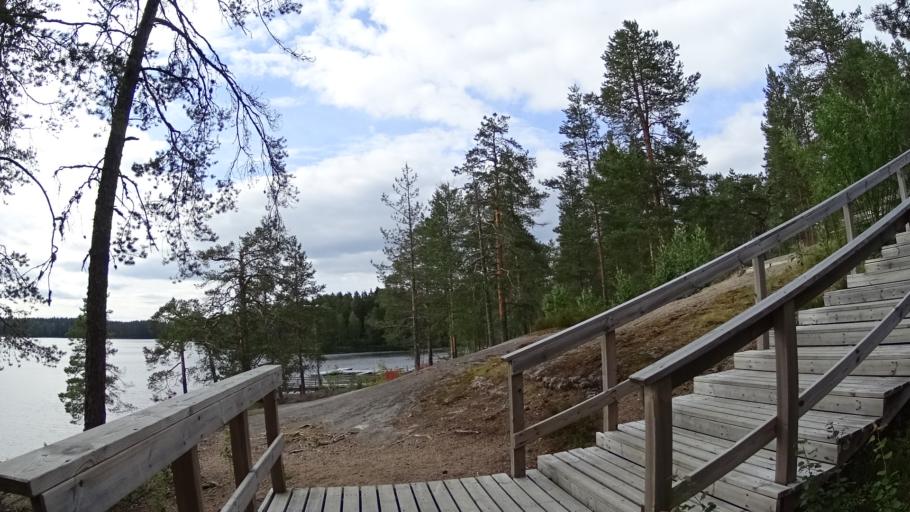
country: FI
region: Southern Ostrobothnia
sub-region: Kuusiokunnat
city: AEhtaeri
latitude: 62.5355
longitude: 24.1793
